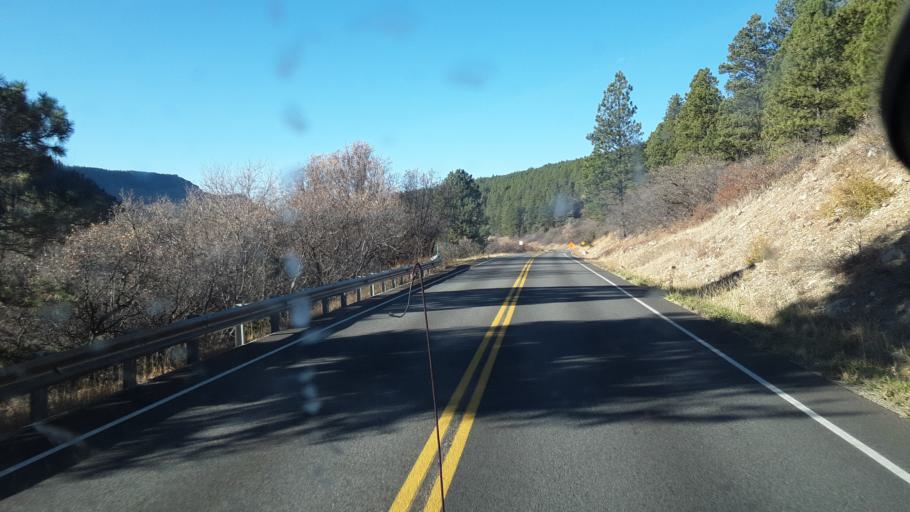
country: US
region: Colorado
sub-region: La Plata County
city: Bayfield
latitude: 37.3462
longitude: -107.7127
